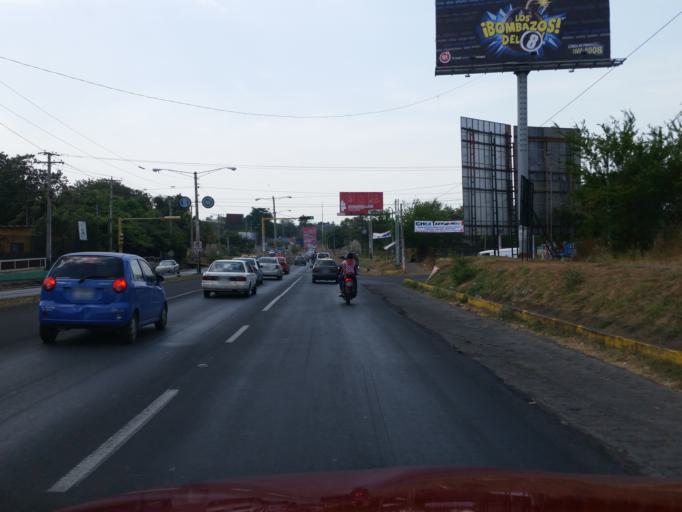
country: NI
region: Managua
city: Managua
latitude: 12.1340
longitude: -86.2678
